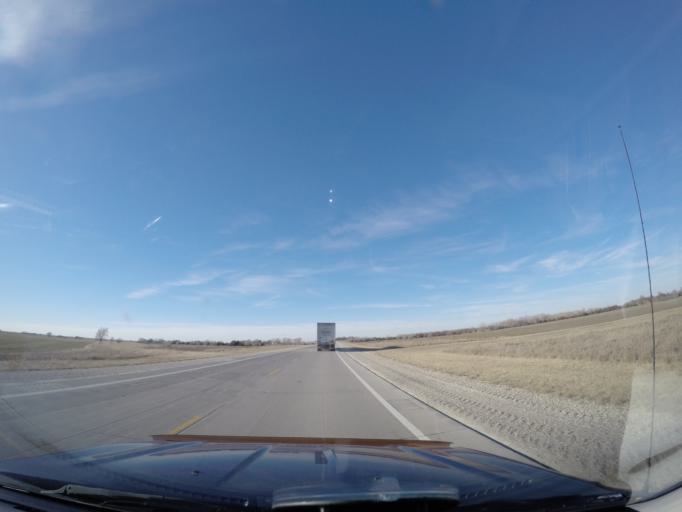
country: US
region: Kansas
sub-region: Marion County
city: Marion
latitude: 38.3573
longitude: -97.1052
